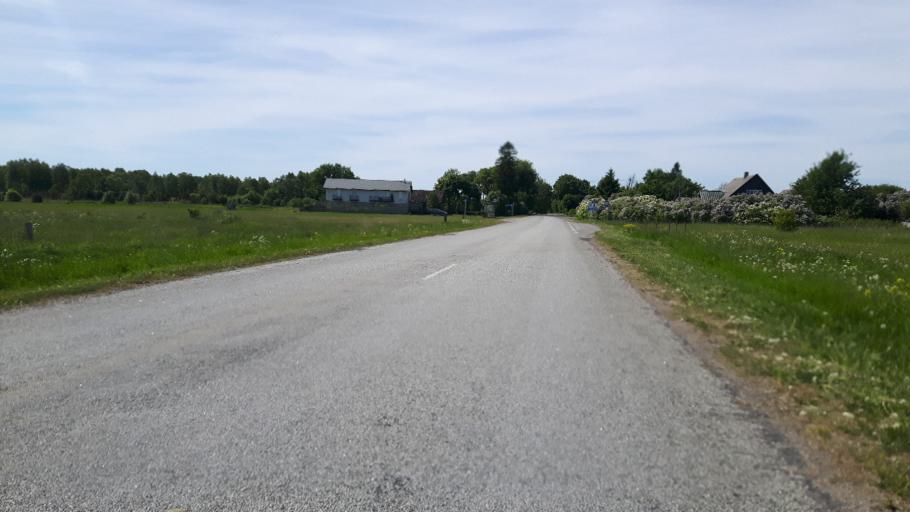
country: EE
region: Harju
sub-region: Kuusalu vald
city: Kuusalu
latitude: 59.4671
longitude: 25.3169
